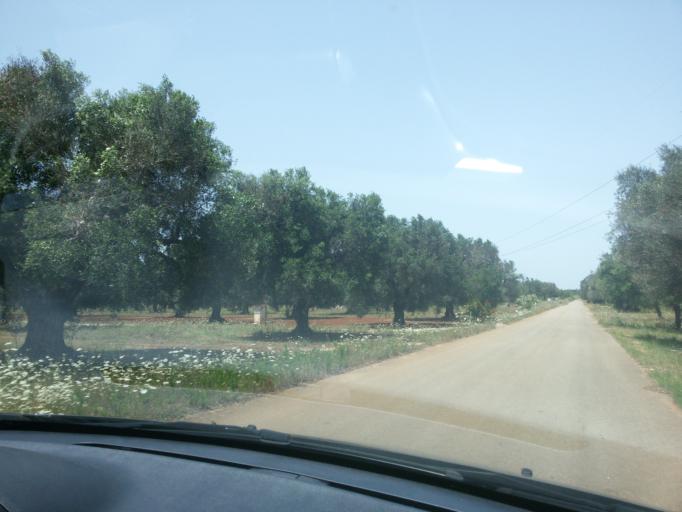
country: IT
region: Apulia
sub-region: Provincia di Lecce
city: Porto Cesareo
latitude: 40.3203
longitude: 17.8941
